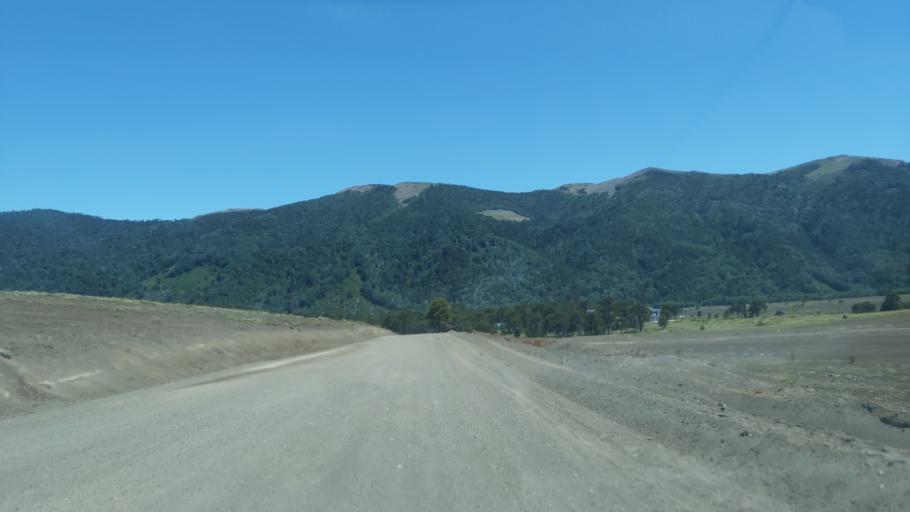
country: CL
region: Araucania
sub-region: Provincia de Cautin
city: Vilcun
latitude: -38.4153
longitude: -71.5423
